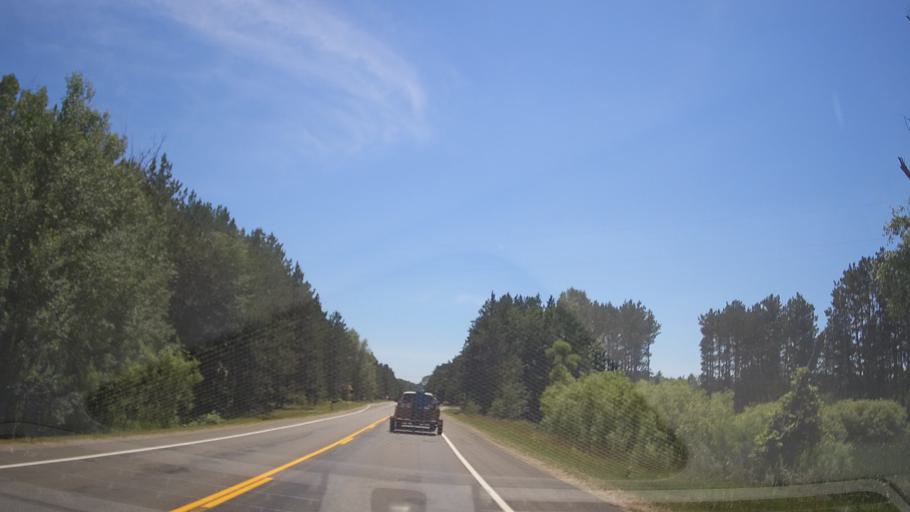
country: US
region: Michigan
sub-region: Grand Traverse County
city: Traverse City
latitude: 44.6484
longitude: -85.6965
